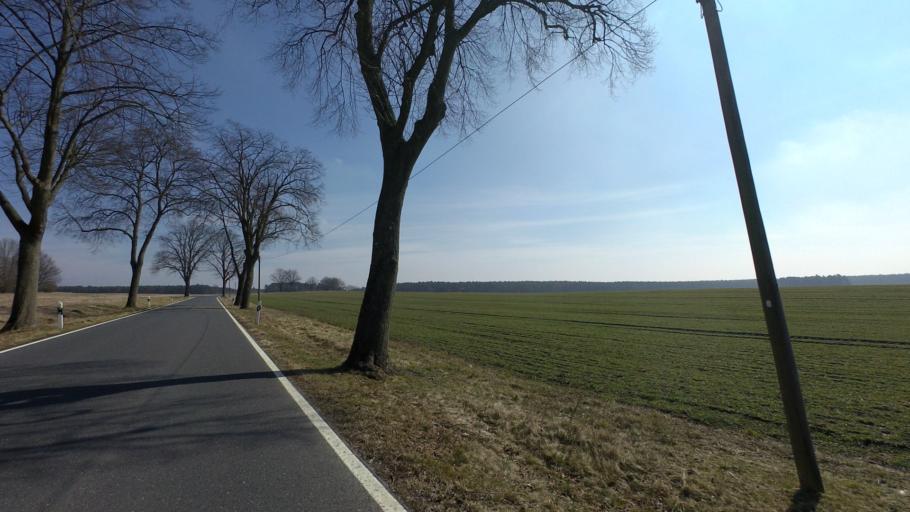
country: DE
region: Saxony-Anhalt
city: Nudersdorf
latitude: 52.0219
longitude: 12.5384
